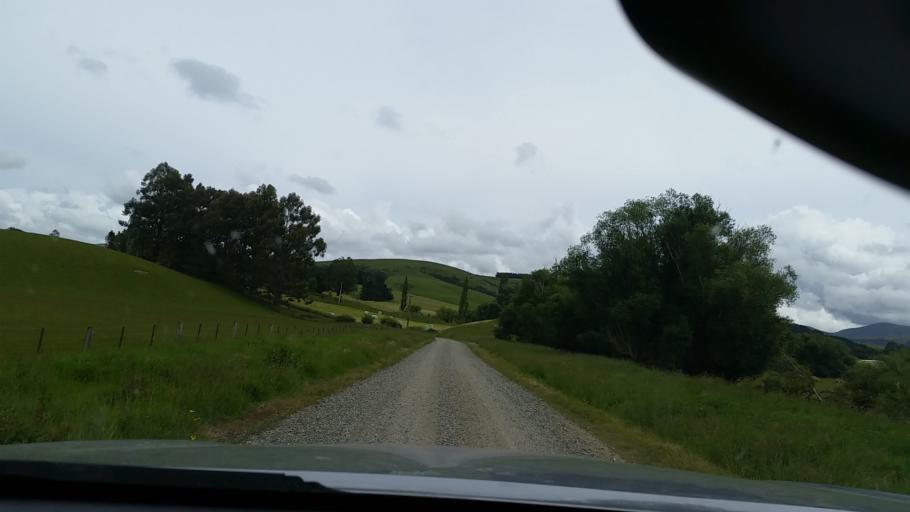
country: NZ
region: Otago
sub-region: Queenstown-Lakes District
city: Kingston
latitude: -45.7275
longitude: 168.7722
